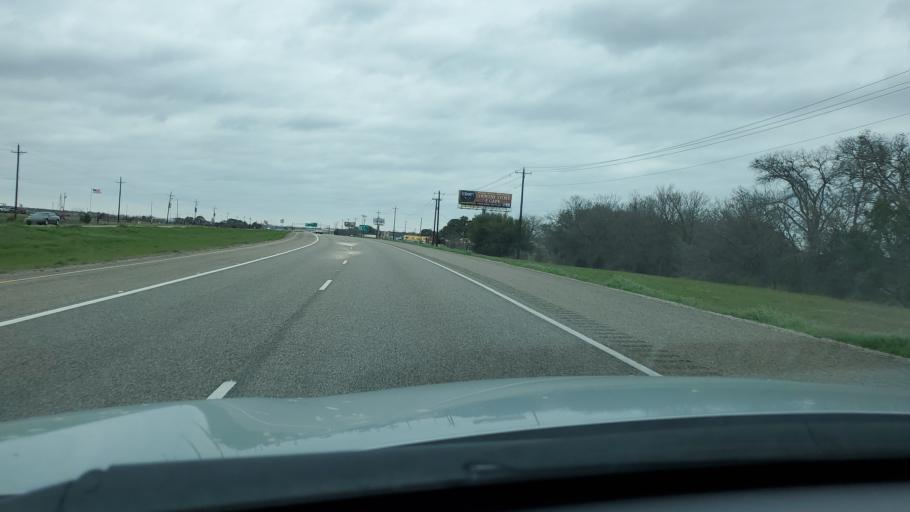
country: US
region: Texas
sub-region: Williamson County
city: Florence
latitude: 30.8124
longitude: -97.7733
